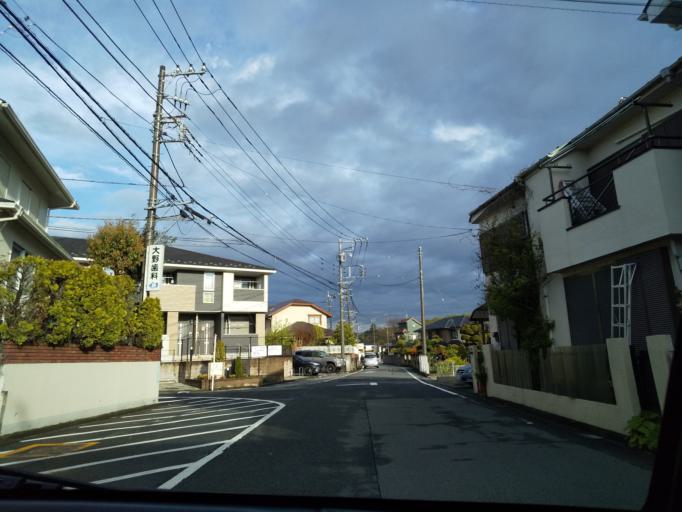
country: JP
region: Tokyo
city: Hachioji
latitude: 35.6033
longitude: 139.3216
